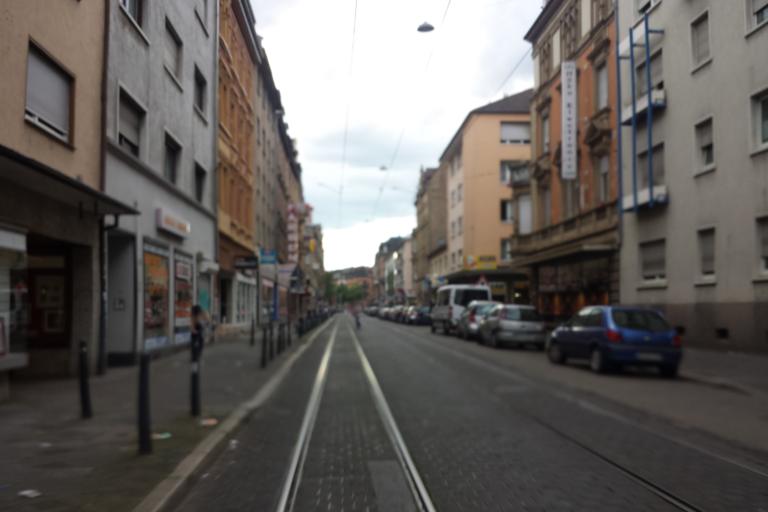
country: DE
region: Baden-Wuerttemberg
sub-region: Karlsruhe Region
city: Mannheim
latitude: 49.4979
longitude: 8.4704
